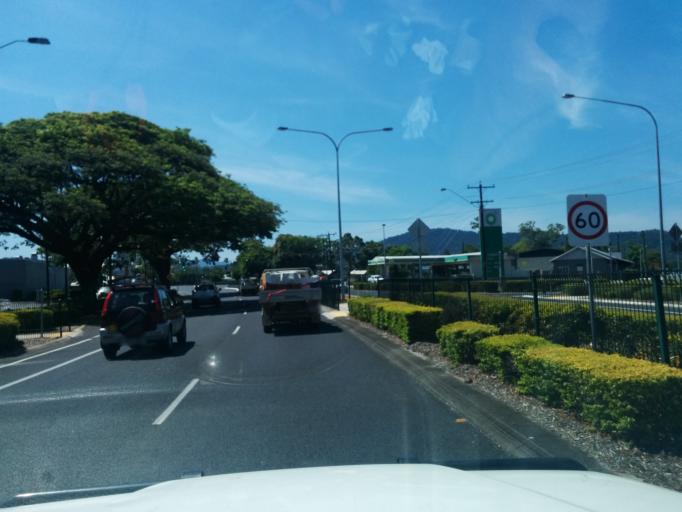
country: AU
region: Queensland
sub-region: Cairns
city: Cairns
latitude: -16.9263
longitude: 145.7418
